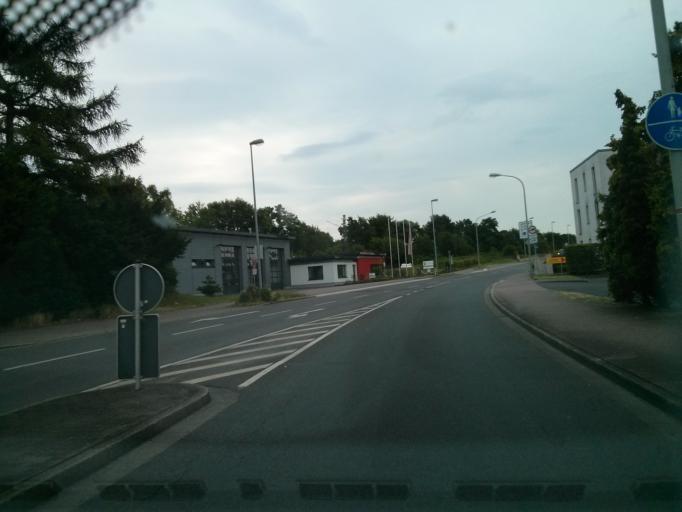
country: DE
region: North Rhine-Westphalia
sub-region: Regierungsbezirk Dusseldorf
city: Krefeld
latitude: 51.3277
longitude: 6.6149
